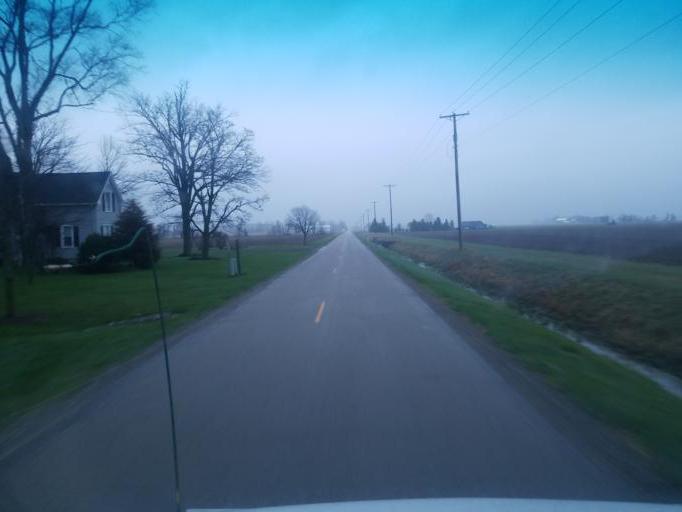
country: US
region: Ohio
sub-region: Fulton County
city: Archbold
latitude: 41.4277
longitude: -84.2801
